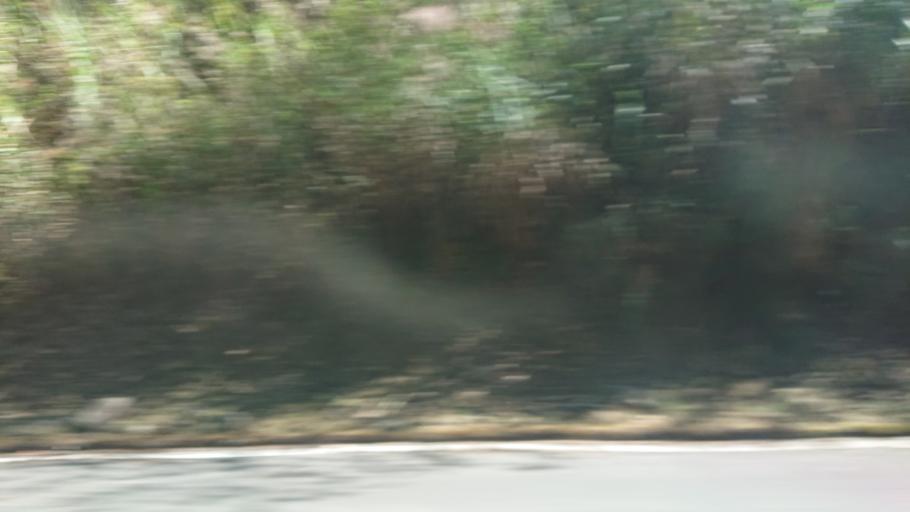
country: TW
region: Taiwan
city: Lugu
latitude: 23.4857
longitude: 120.8525
